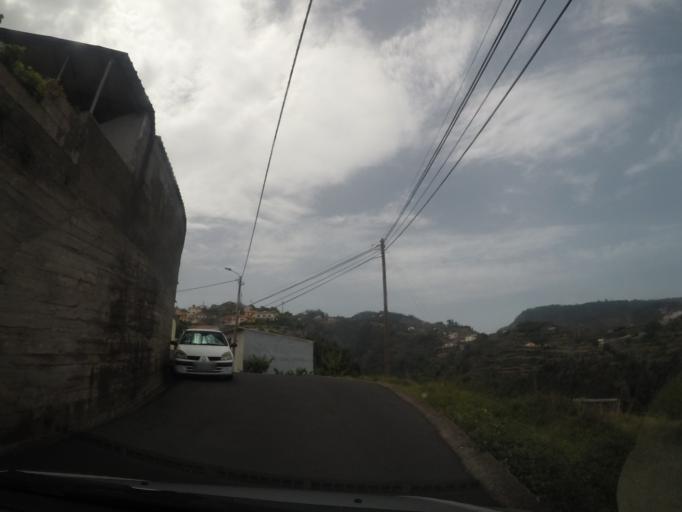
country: PT
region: Madeira
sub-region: Santa Cruz
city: Santa Cruz
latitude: 32.6864
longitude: -16.8065
